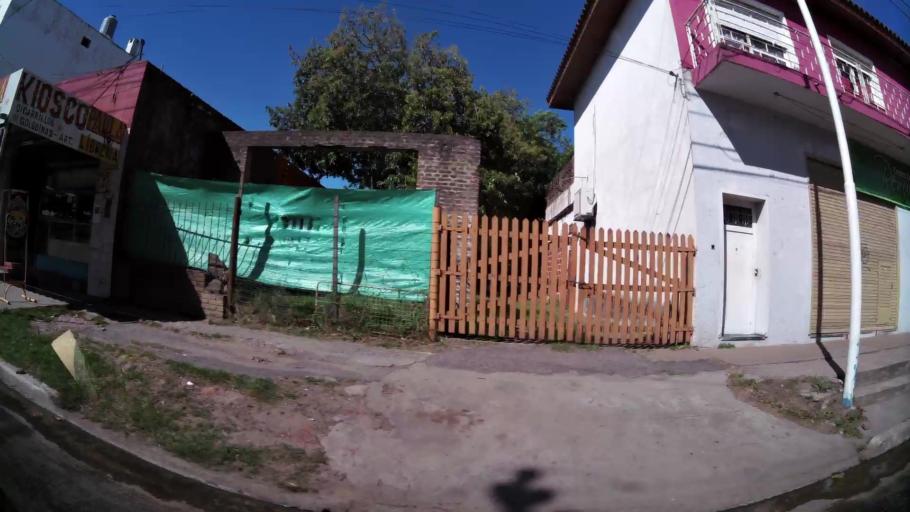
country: AR
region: Buenos Aires
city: Santa Catalina - Dique Lujan
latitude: -34.4846
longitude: -58.6970
